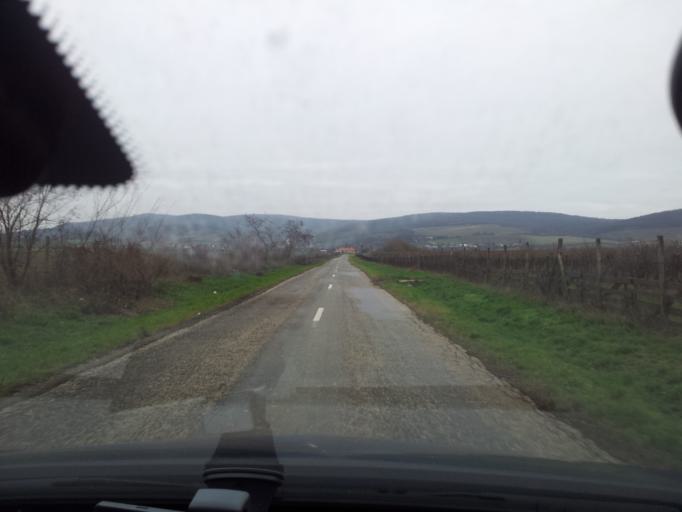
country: HU
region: Borsod-Abauj-Zemplen
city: Satoraljaujhely
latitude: 48.4493
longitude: 21.6658
